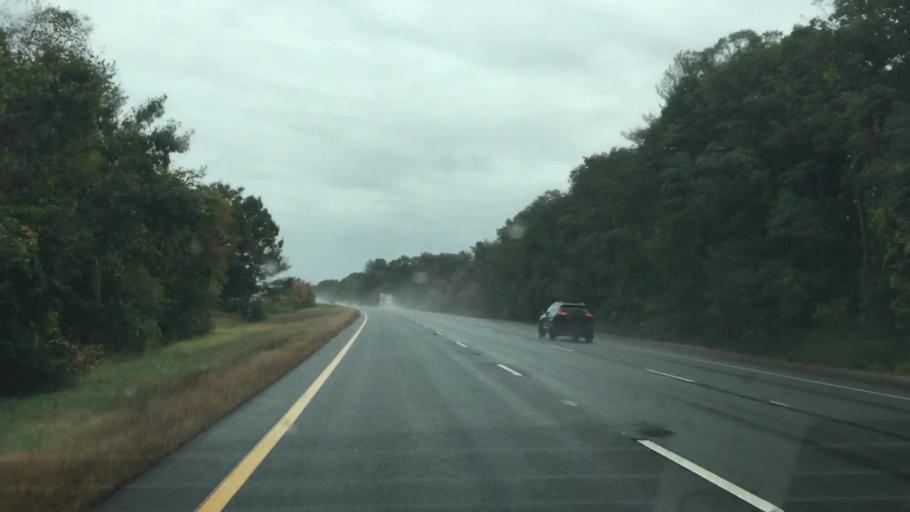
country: US
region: Massachusetts
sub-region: Essex County
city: Merrimac
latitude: 42.8346
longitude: -70.9640
